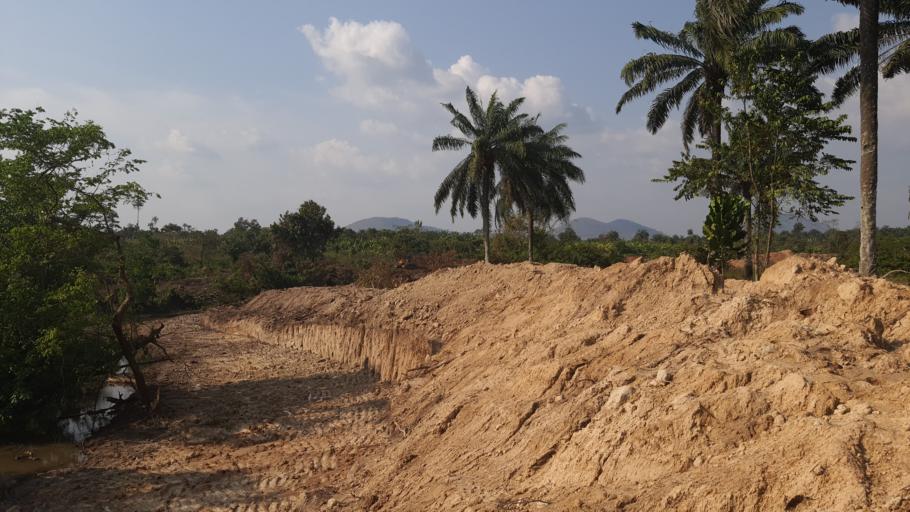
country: NG
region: Osun
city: Iwo
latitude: 7.7103
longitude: 4.1115
